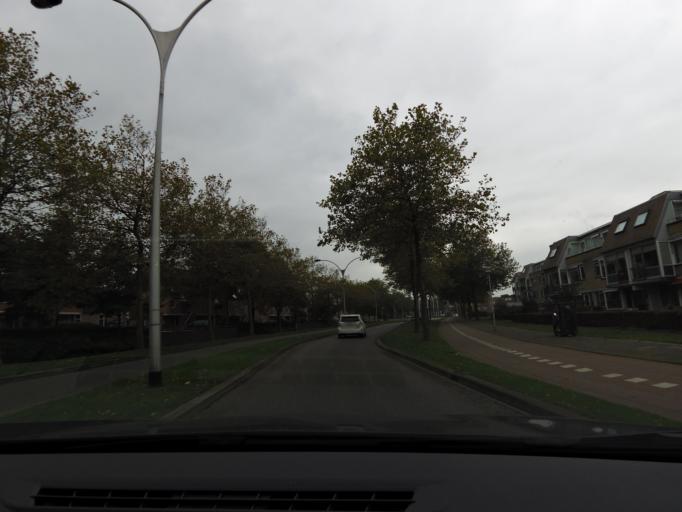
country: NL
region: South Holland
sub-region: Gemeente Hellevoetsluis
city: Hellevoetsluis
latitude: 51.8316
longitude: 4.1505
